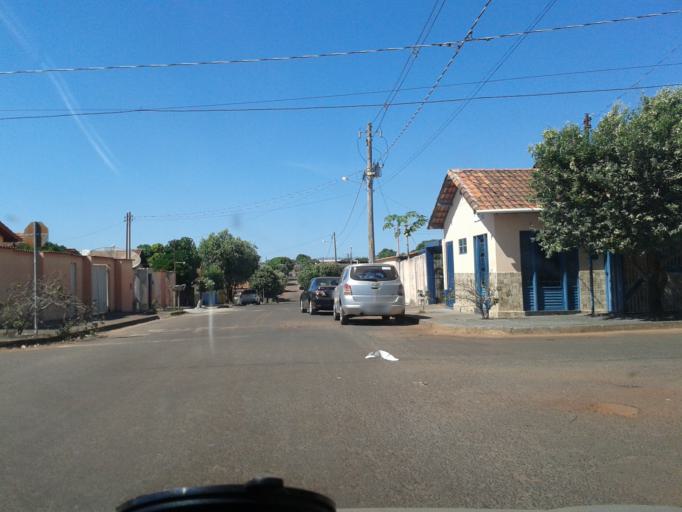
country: BR
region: Goias
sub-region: Sao Miguel Do Araguaia
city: Sao Miguel do Araguaia
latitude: -13.2786
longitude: -50.1575
